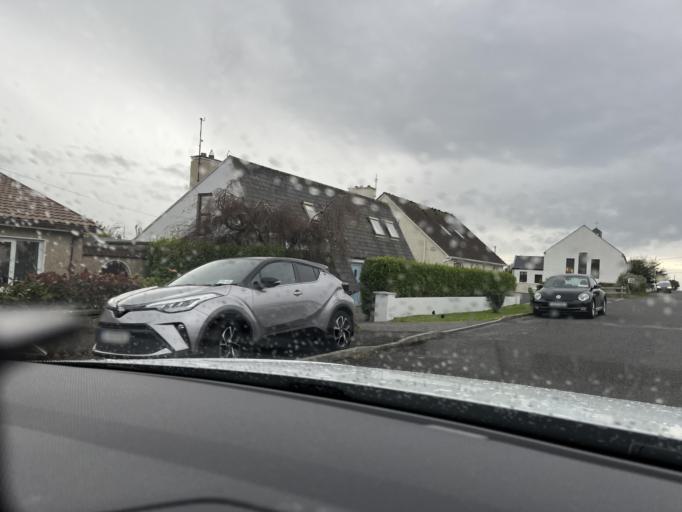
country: IE
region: Connaught
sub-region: Sligo
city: Strandhill
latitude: 54.3082
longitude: -8.5527
